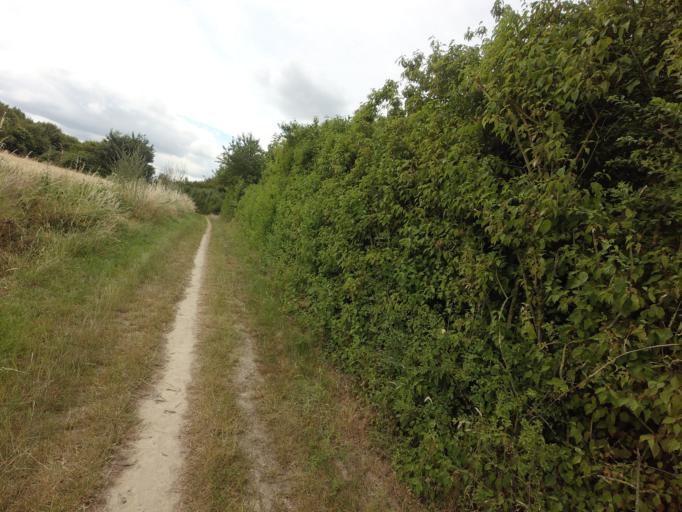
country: NL
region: Limburg
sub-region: Valkenburg aan de Geul
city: Berg
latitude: 50.8546
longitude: 5.7651
